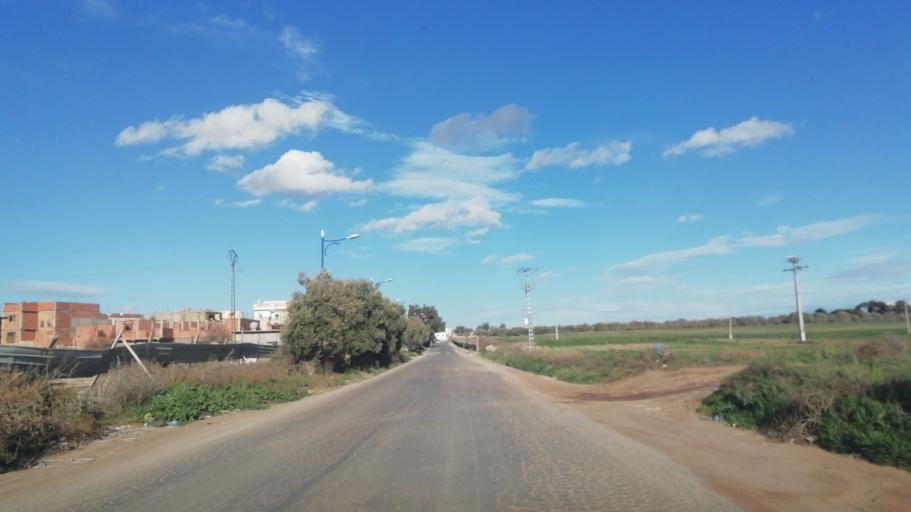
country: DZ
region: Oran
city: Sidi ech Chahmi
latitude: 35.6535
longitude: -0.5282
